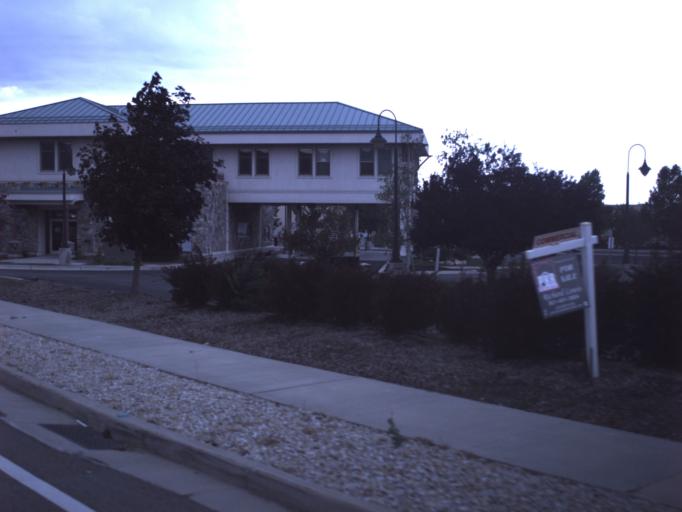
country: US
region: Utah
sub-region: Salt Lake County
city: Draper
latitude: 40.5269
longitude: -111.8946
